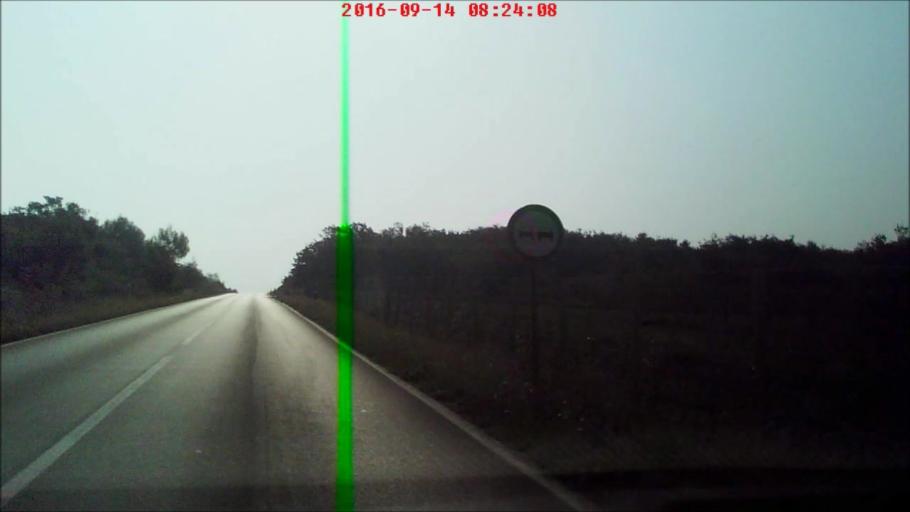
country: HR
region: Zadarska
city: Vrsi
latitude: 44.2079
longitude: 15.2398
